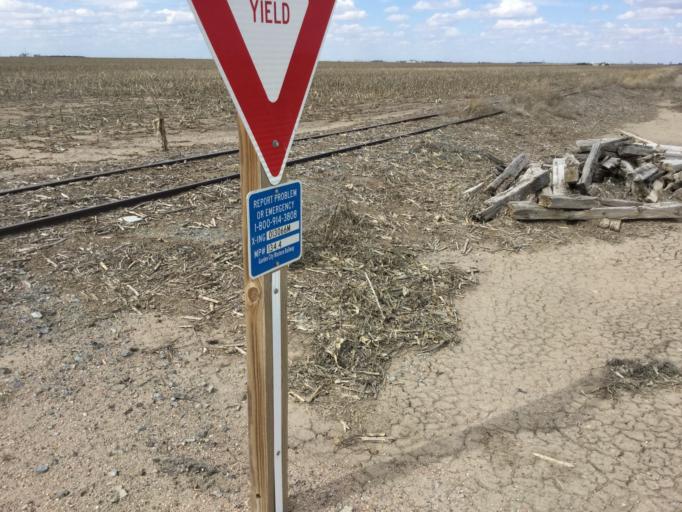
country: US
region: Kansas
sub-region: Scott County
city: Scott City
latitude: 38.2797
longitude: -100.9113
